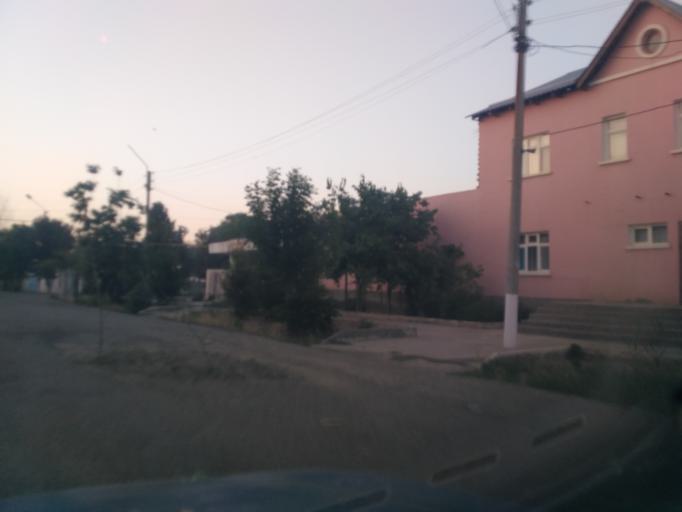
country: UZ
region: Sirdaryo
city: Guliston
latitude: 40.4997
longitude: 68.7700
